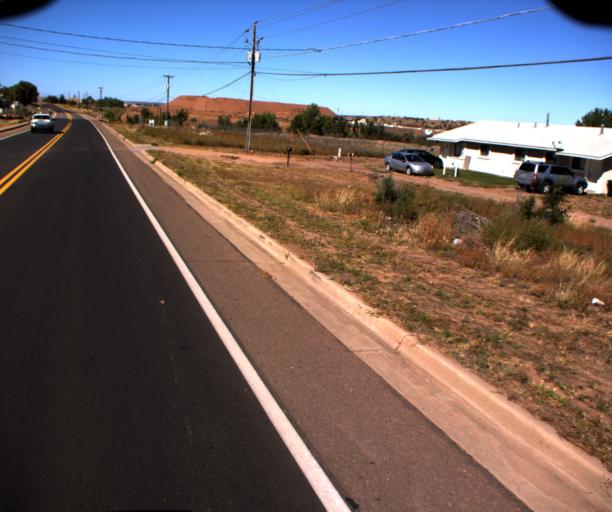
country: US
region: Arizona
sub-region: Navajo County
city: Snowflake
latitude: 34.5134
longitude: -110.0825
